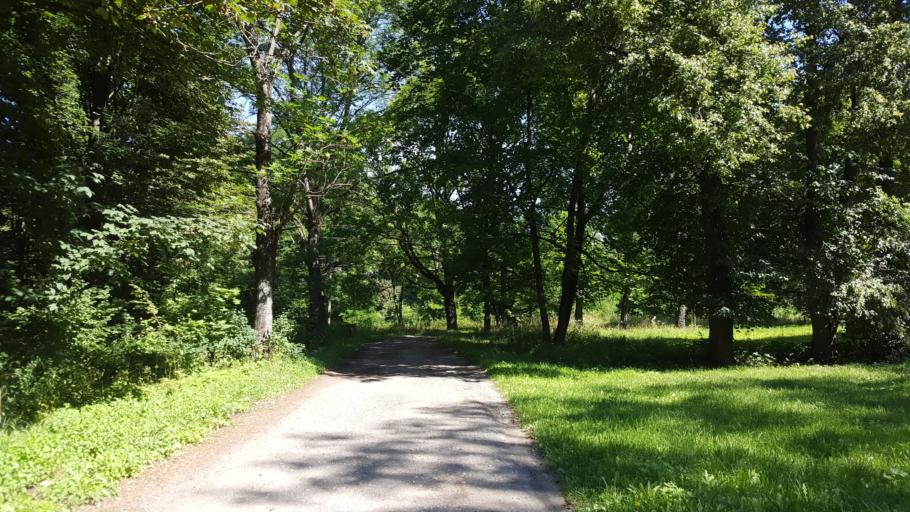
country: BY
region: Brest
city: Kamyanyets
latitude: 52.3844
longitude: 23.6545
